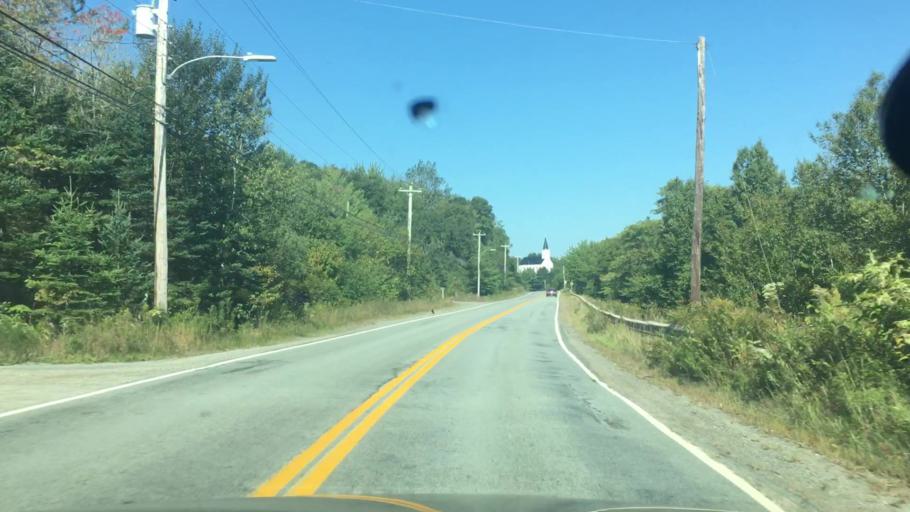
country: CA
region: Nova Scotia
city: New Glasgow
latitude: 44.9191
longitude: -62.5429
